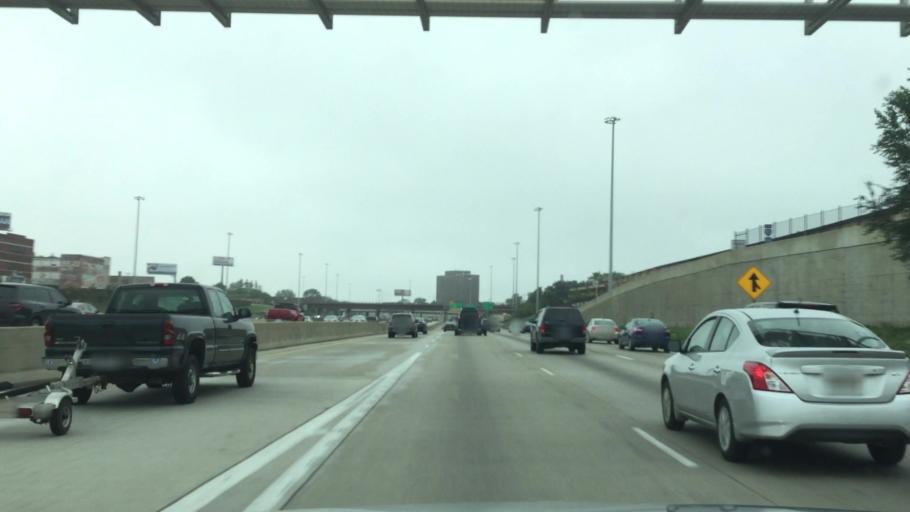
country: US
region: Illinois
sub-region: Cook County
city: Chicago
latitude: 41.7861
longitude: -87.6316
